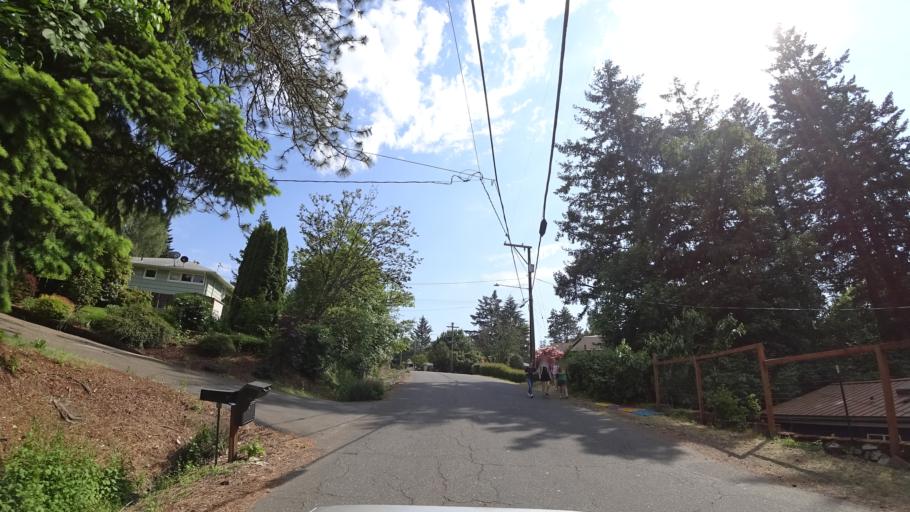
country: US
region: Oregon
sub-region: Washington County
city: Garden Home-Whitford
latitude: 45.4566
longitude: -122.7407
